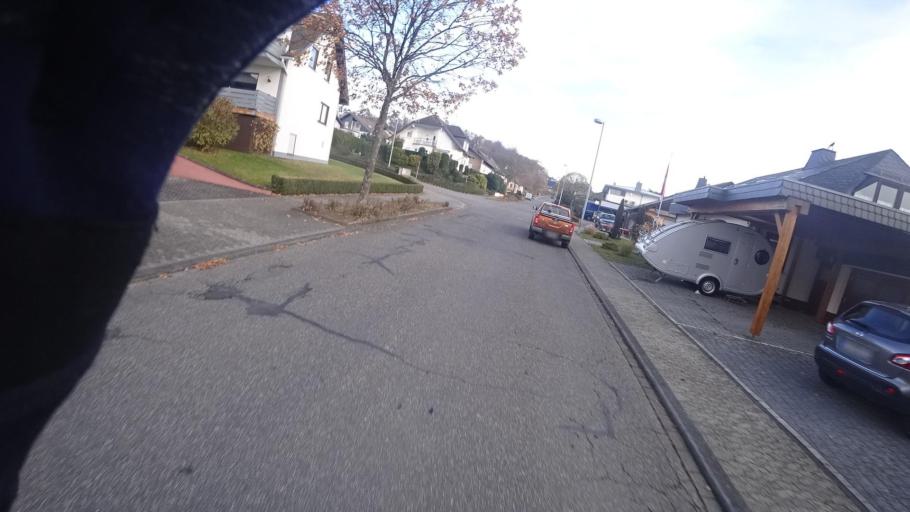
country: DE
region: Rheinland-Pfalz
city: Schwall
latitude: 50.1498
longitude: 7.5452
